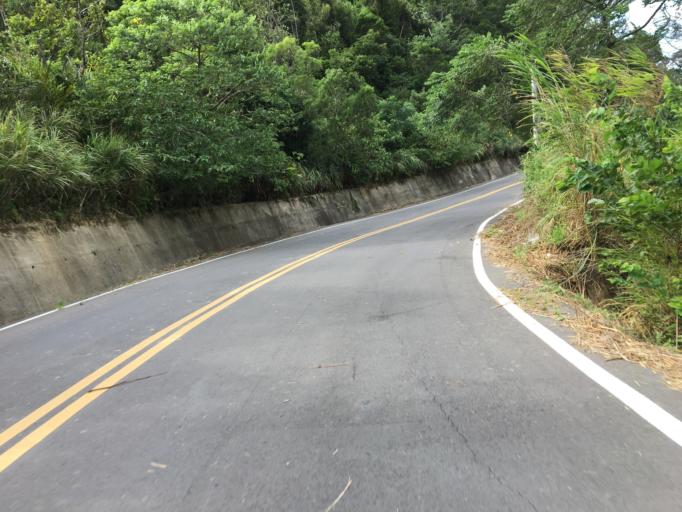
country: TW
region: Taiwan
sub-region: Hsinchu
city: Hsinchu
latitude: 24.7065
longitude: 120.9527
